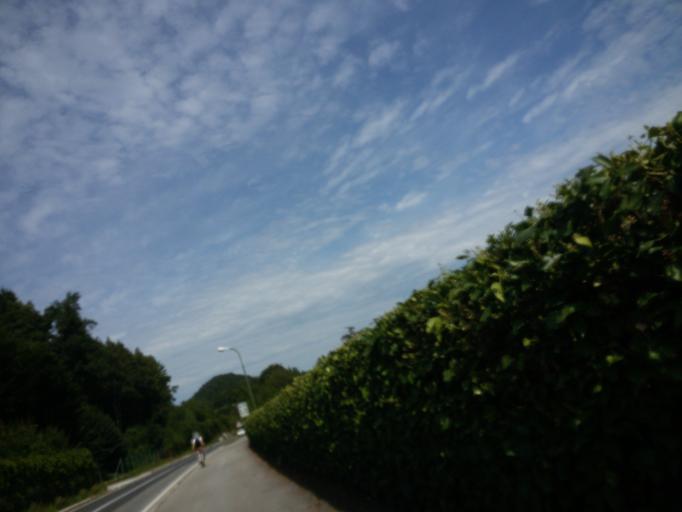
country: AT
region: Carinthia
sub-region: Politischer Bezirk Klagenfurt Land
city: Schiefling am See
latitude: 46.6325
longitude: 14.1060
